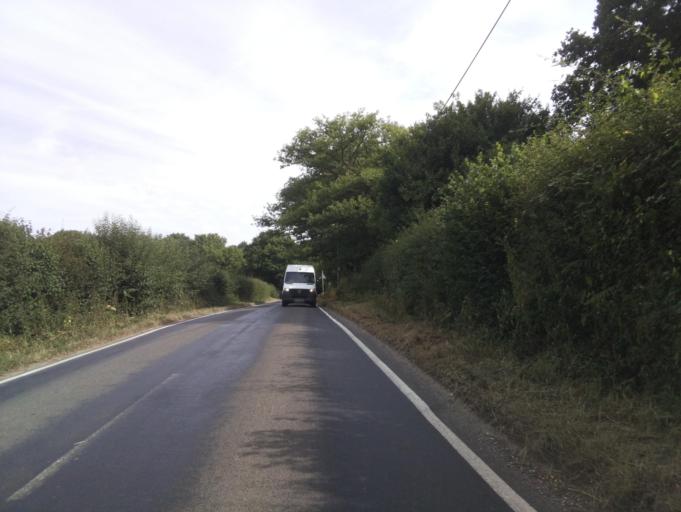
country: GB
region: England
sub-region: Surrey
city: Godstone
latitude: 51.1929
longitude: -0.0660
